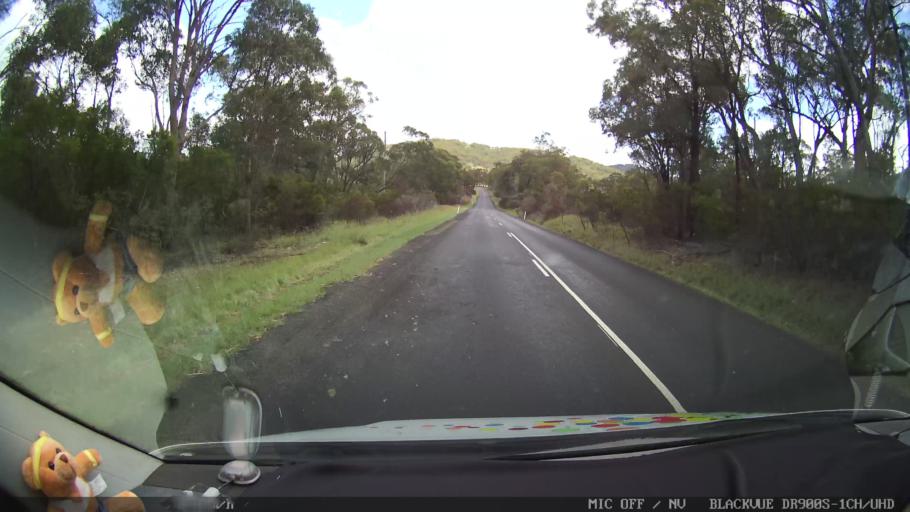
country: AU
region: New South Wales
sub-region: Glen Innes Severn
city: Glen Innes
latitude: -29.5414
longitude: 151.6703
